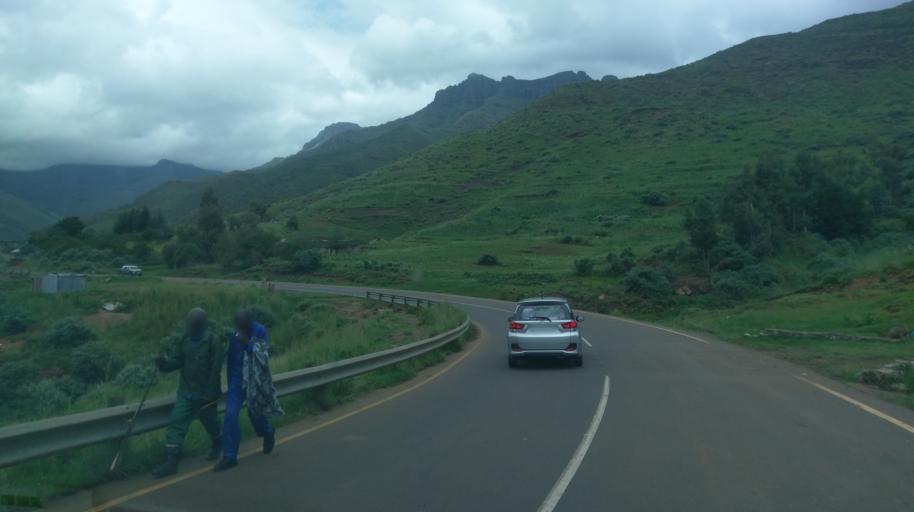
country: LS
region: Butha-Buthe
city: Butha-Buthe
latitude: -29.0482
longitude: 28.3243
